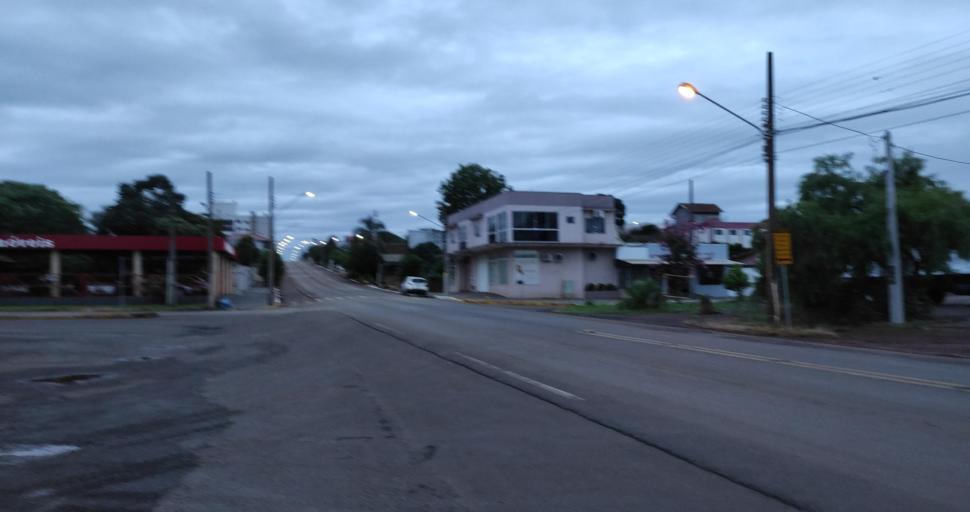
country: BR
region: Parana
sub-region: Clevelandia
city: Clevelandia
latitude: -26.5642
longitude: -52.5321
